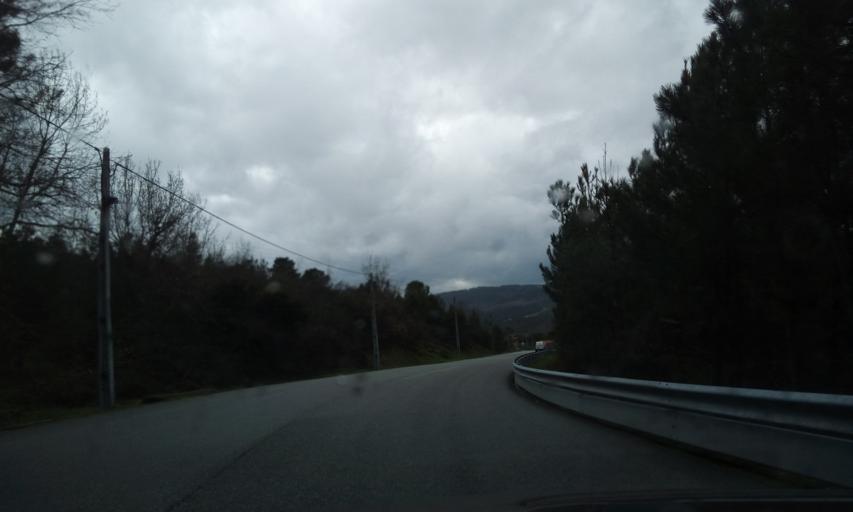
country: PT
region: Viseu
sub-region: Viseu
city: Rio de Loba
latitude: 40.6052
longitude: -7.8495
